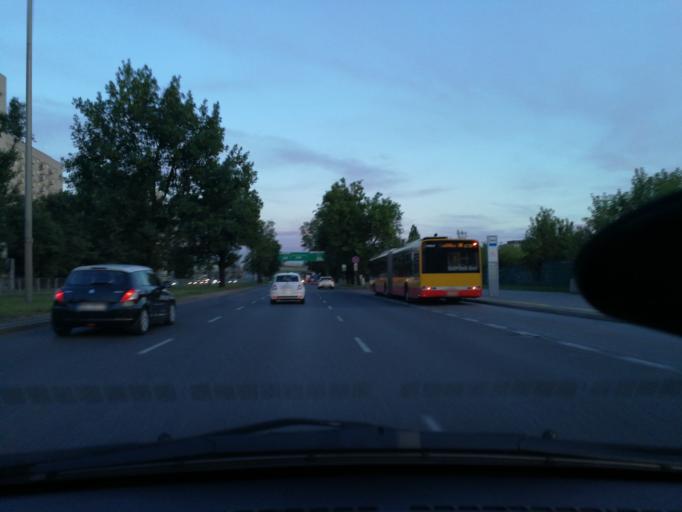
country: PL
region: Masovian Voivodeship
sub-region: Warszawa
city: Mokotow
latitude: 52.2018
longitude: 21.0498
